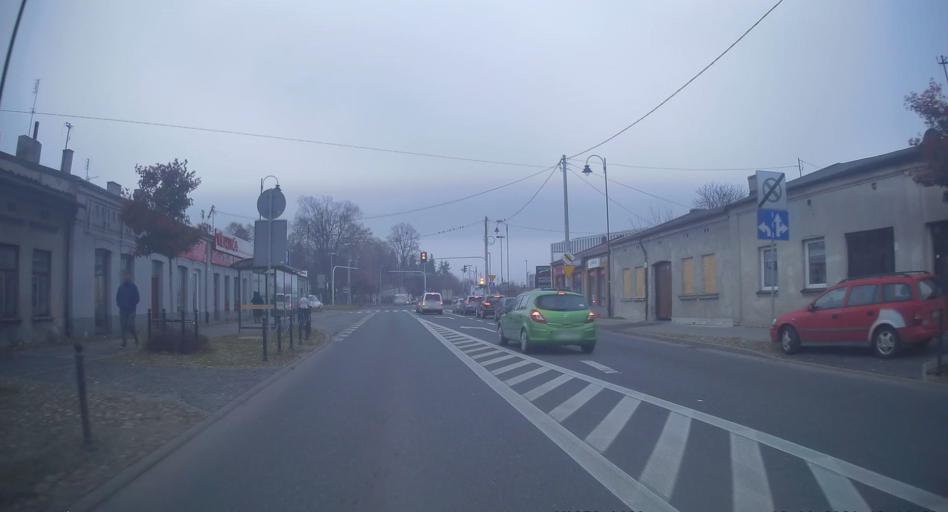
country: PL
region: Silesian Voivodeship
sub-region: Czestochowa
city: Czestochowa
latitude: 50.8186
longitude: 19.0887
